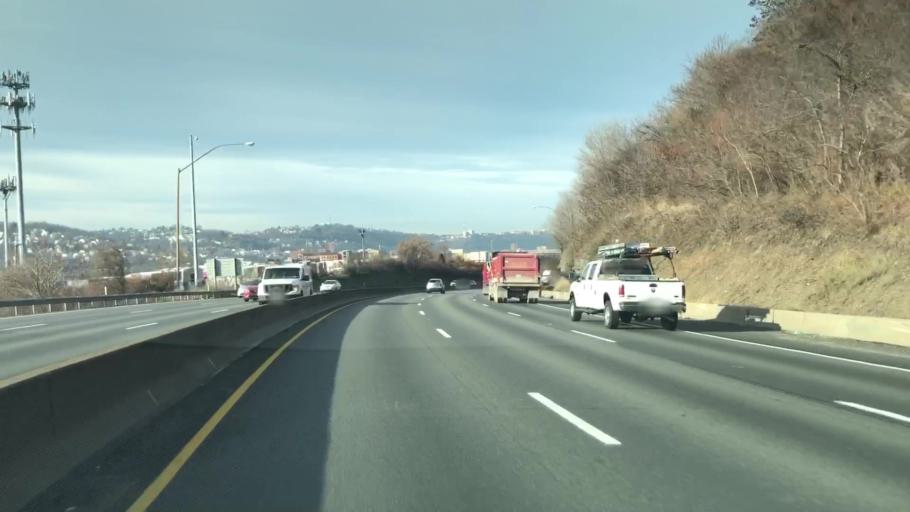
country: US
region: Pennsylvania
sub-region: Allegheny County
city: Bloomfield
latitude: 40.4280
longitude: -79.9512
